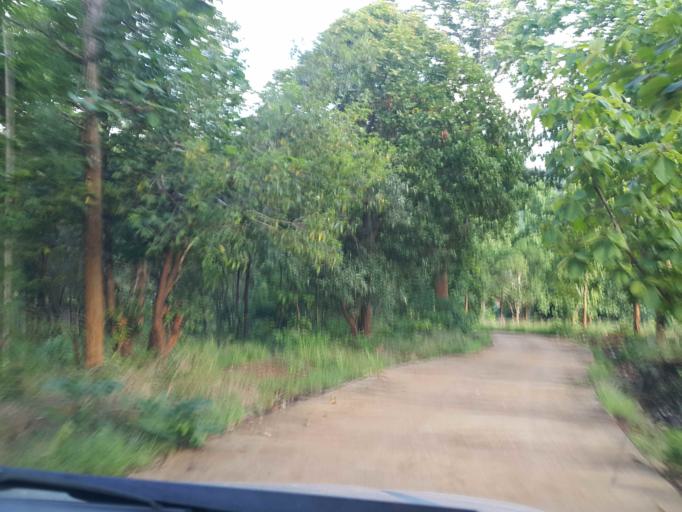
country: TH
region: Chiang Mai
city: Mae Chaem
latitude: 18.4980
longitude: 98.3963
